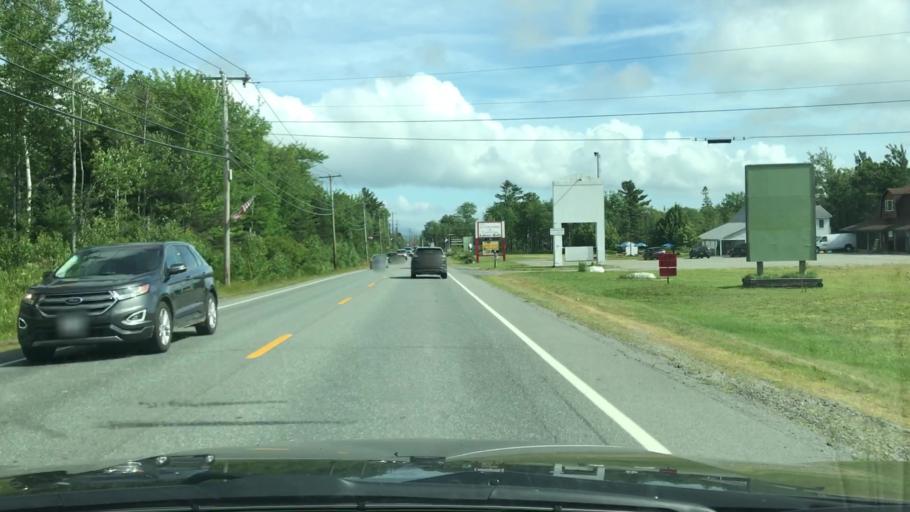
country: US
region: Maine
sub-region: Hancock County
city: Ellsworth
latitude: 44.5048
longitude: -68.3865
